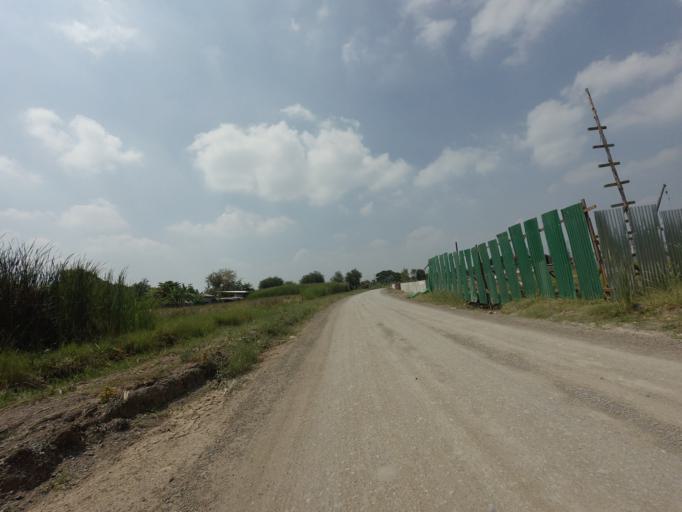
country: TH
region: Bangkok
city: Saphan Sung
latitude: 13.7518
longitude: 100.6738
